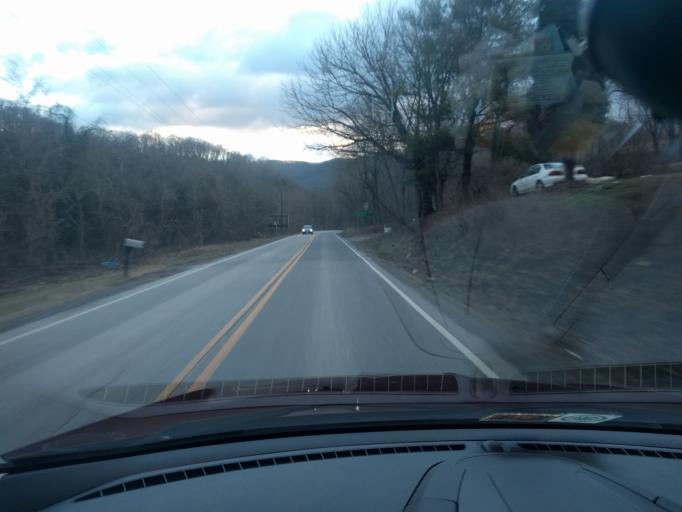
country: US
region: Virginia
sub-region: Botetourt County
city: Buchanan
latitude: 37.5297
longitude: -79.6735
